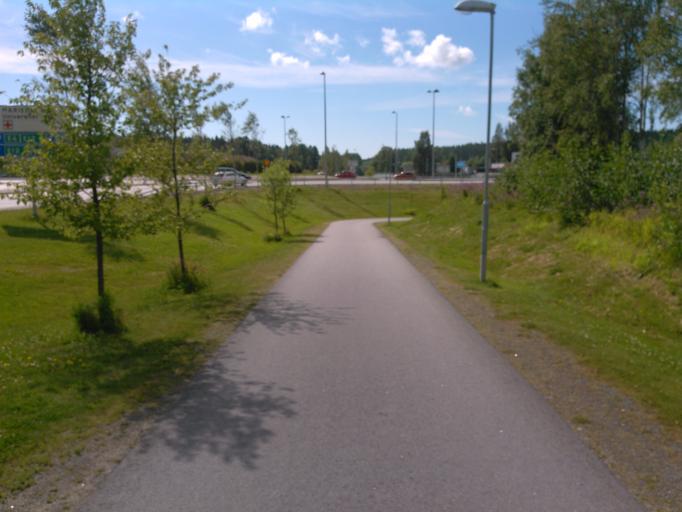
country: SE
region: Vaesterbotten
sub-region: Umea Kommun
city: Ersmark
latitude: 63.8493
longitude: 20.3143
